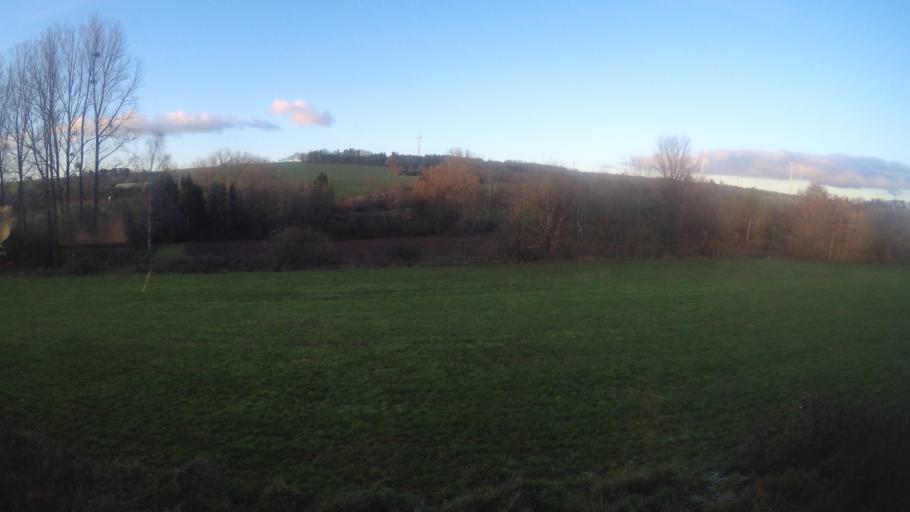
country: DE
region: Saarland
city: Ottweiler
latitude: 49.4172
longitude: 7.1975
